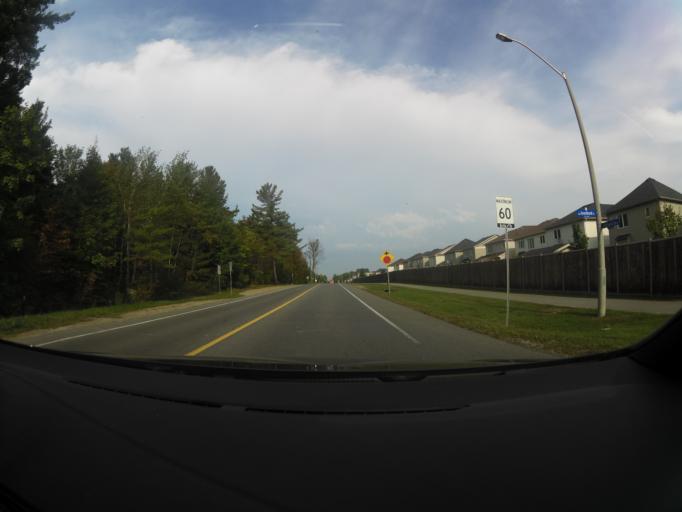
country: CA
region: Ontario
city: Bells Corners
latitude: 45.3447
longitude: -75.9443
